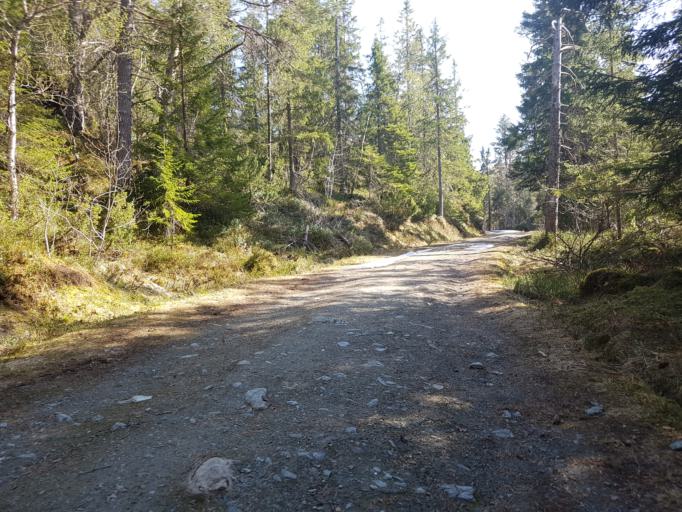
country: NO
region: Sor-Trondelag
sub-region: Trondheim
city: Trondheim
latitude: 63.4330
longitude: 10.2928
